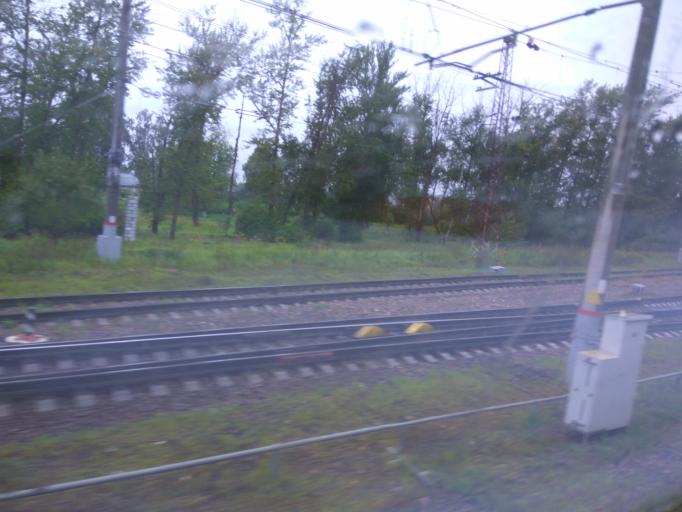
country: RU
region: Moskovskaya
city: Zhilevo
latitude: 54.9840
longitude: 38.0324
